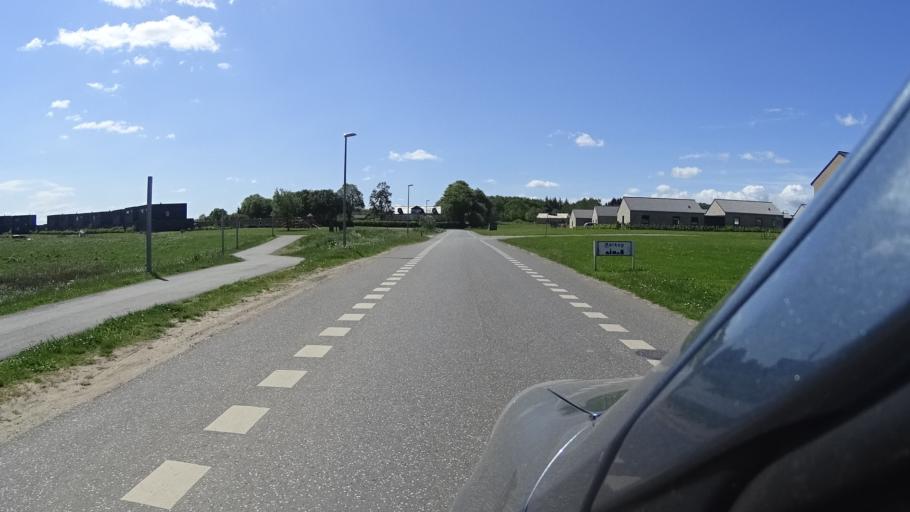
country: DK
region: South Denmark
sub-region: Vejle Kommune
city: Borkop
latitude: 55.6336
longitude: 9.6466
